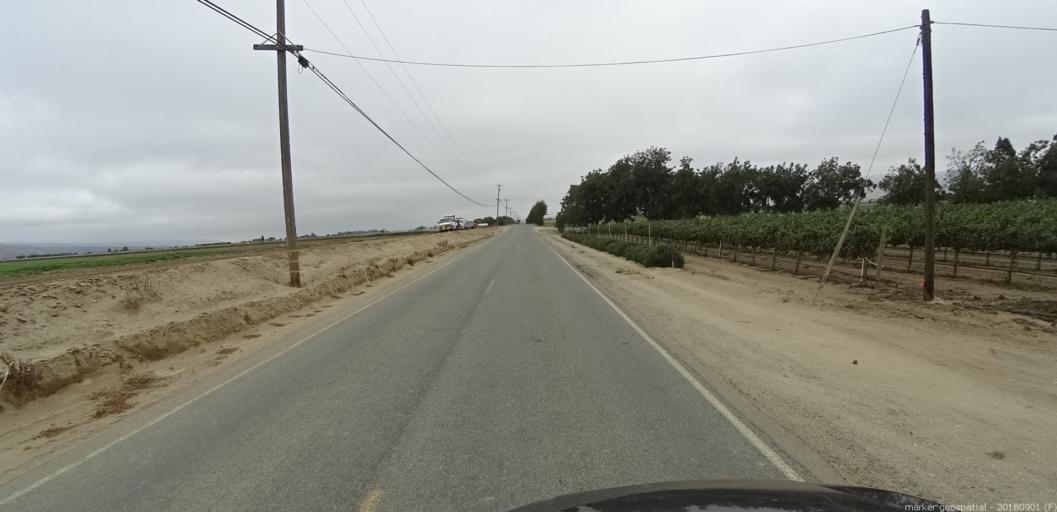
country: US
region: California
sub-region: Monterey County
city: Soledad
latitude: 36.3864
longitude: -121.3312
